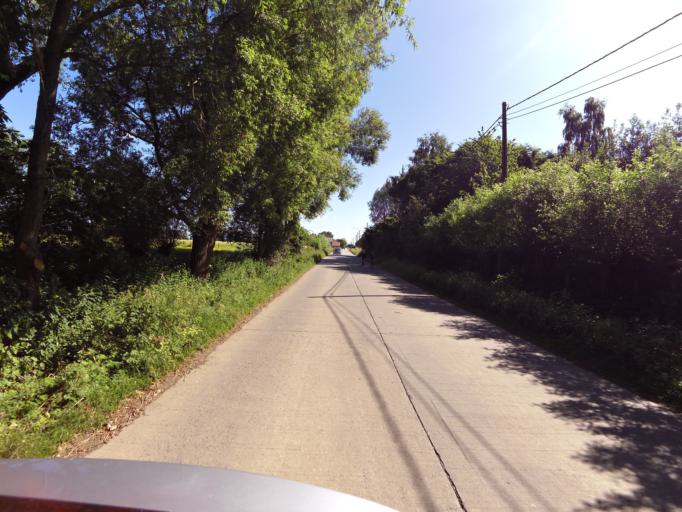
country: BE
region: Flanders
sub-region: Provincie West-Vlaanderen
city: Koekelare
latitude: 51.0376
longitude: 2.9680
